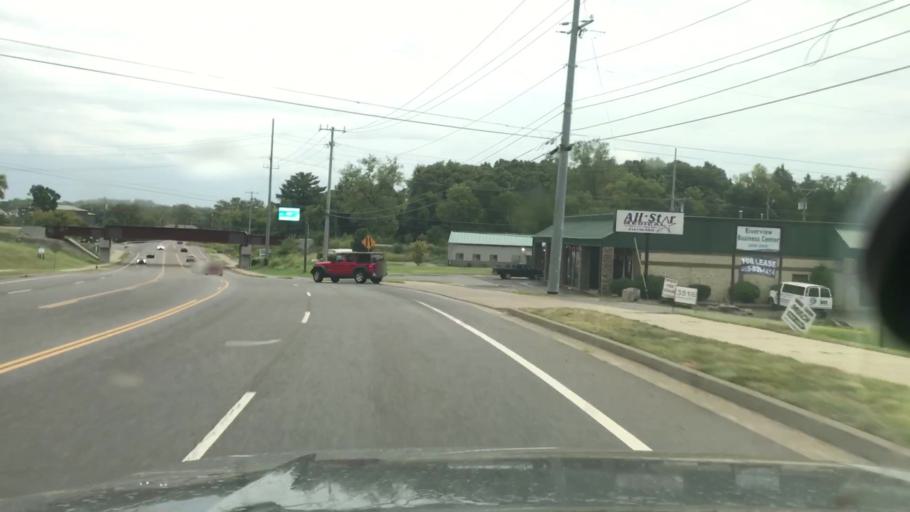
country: US
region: Tennessee
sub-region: Davidson County
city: Lakewood
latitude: 36.1863
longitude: -86.6302
